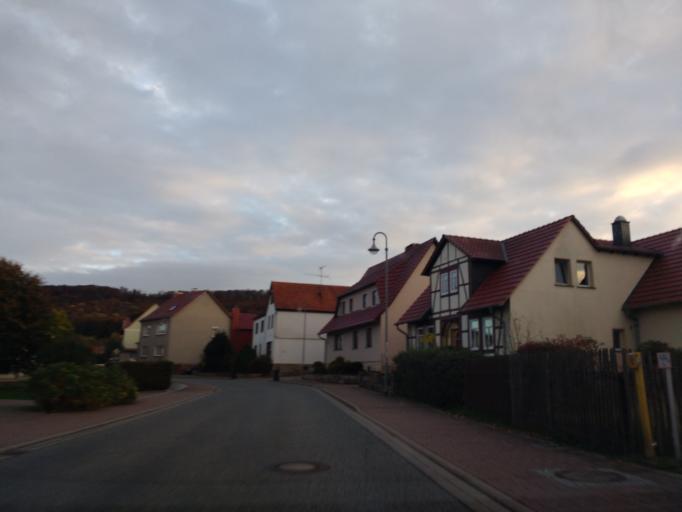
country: DE
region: Thuringia
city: Kleinbartloff
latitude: 51.3530
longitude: 10.3826
